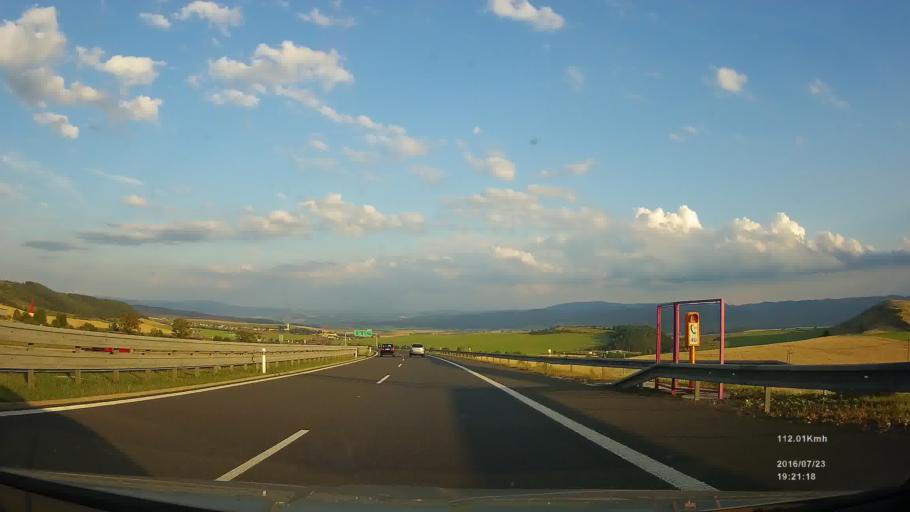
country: SK
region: Presovsky
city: Lubica
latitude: 49.0232
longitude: 20.4372
